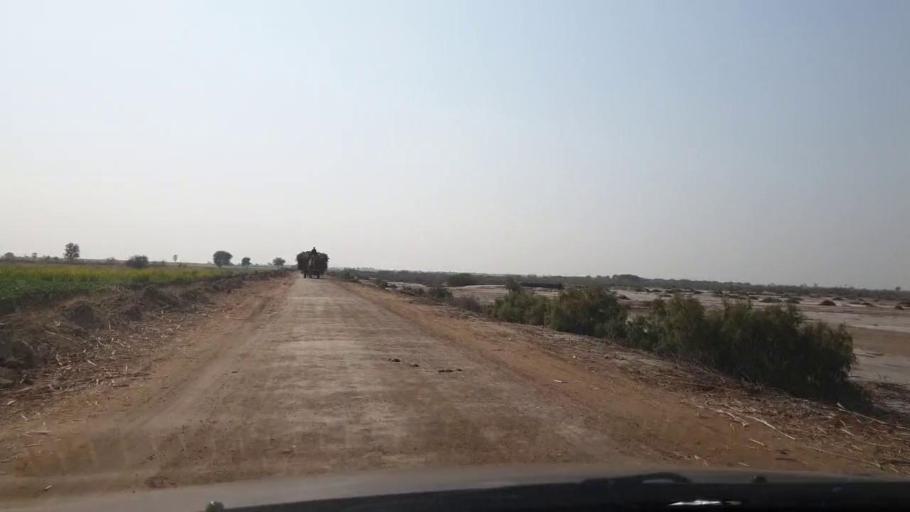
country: PK
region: Sindh
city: Jhol
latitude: 25.8586
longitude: 68.9933
